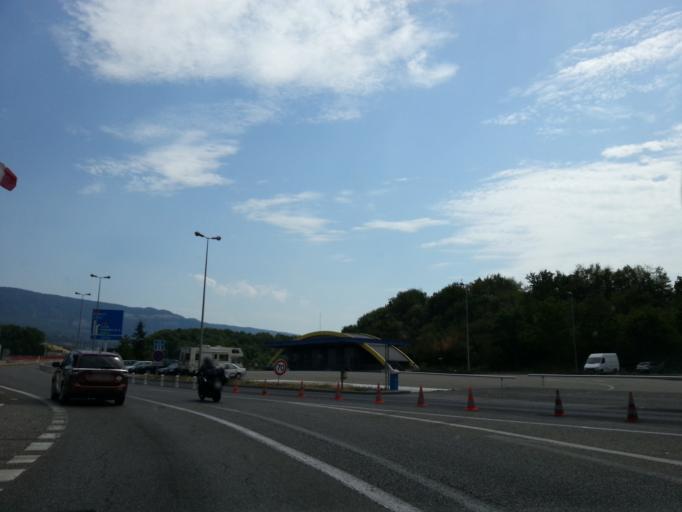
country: FR
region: Rhone-Alpes
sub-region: Departement de la Haute-Savoie
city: Saint-Julien-en-Genevois
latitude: 46.1464
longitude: 6.0955
